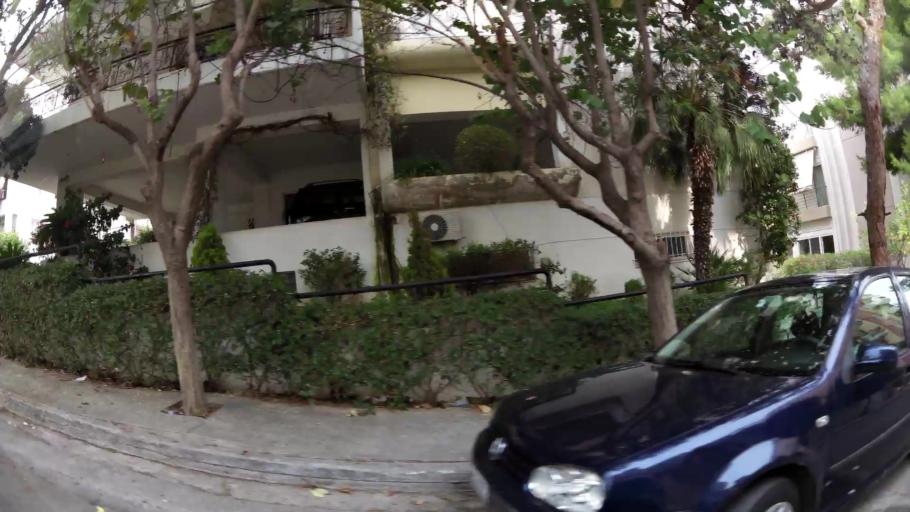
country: GR
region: Attica
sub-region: Nomarchia Athinas
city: Agios Dimitrios
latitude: 37.9228
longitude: 23.7360
